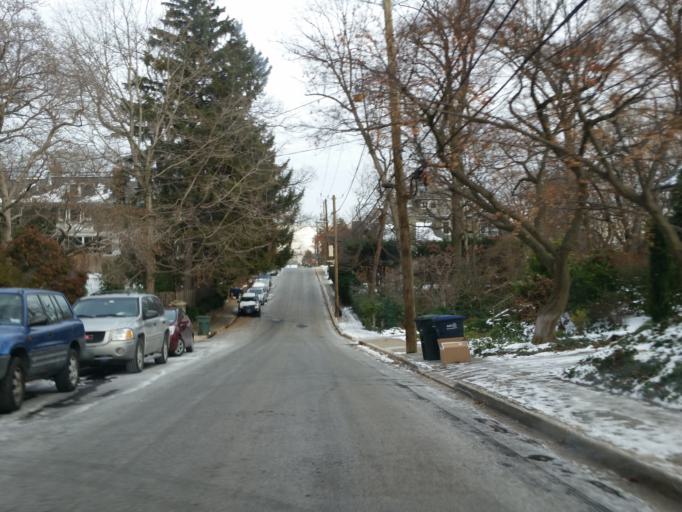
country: US
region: Maryland
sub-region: Montgomery County
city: Friendship Village
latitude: 38.9346
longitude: -77.0639
